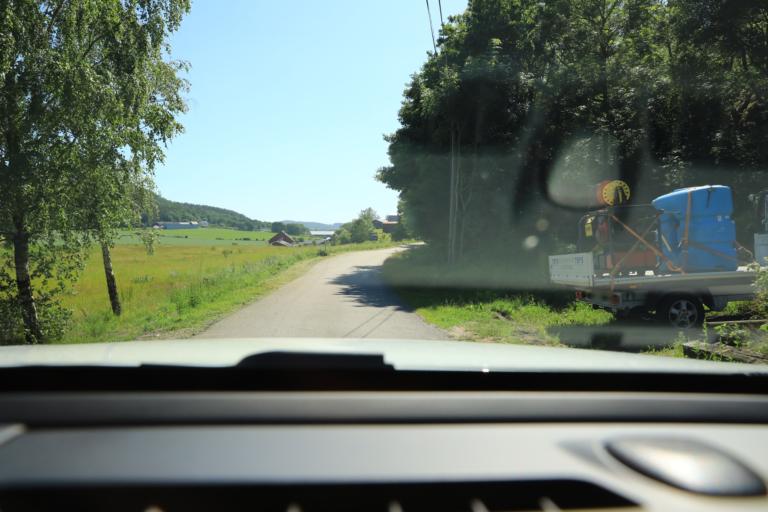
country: SE
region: Halland
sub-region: Varbergs Kommun
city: Veddige
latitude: 57.1905
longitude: 12.3229
